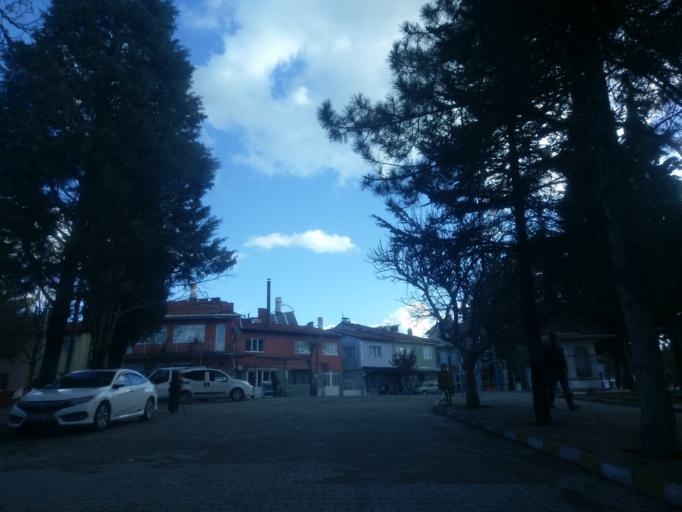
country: TR
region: Kuetahya
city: Gediz
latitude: 38.9930
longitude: 29.3941
